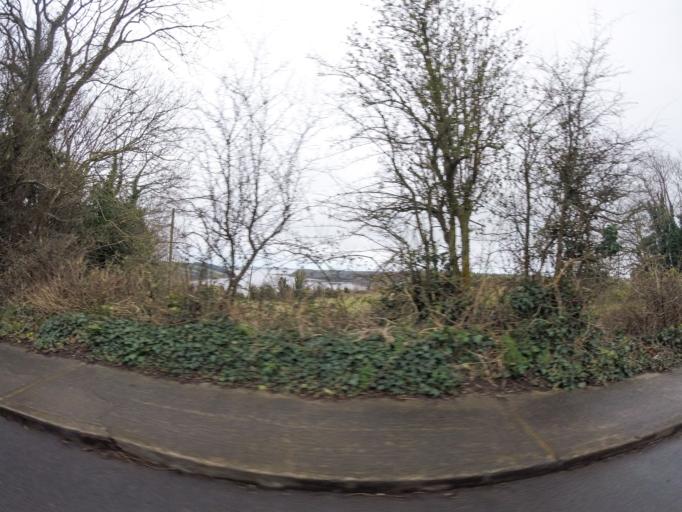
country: IE
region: Munster
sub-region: Waterford
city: Waterford
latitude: 52.2623
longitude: -7.0016
